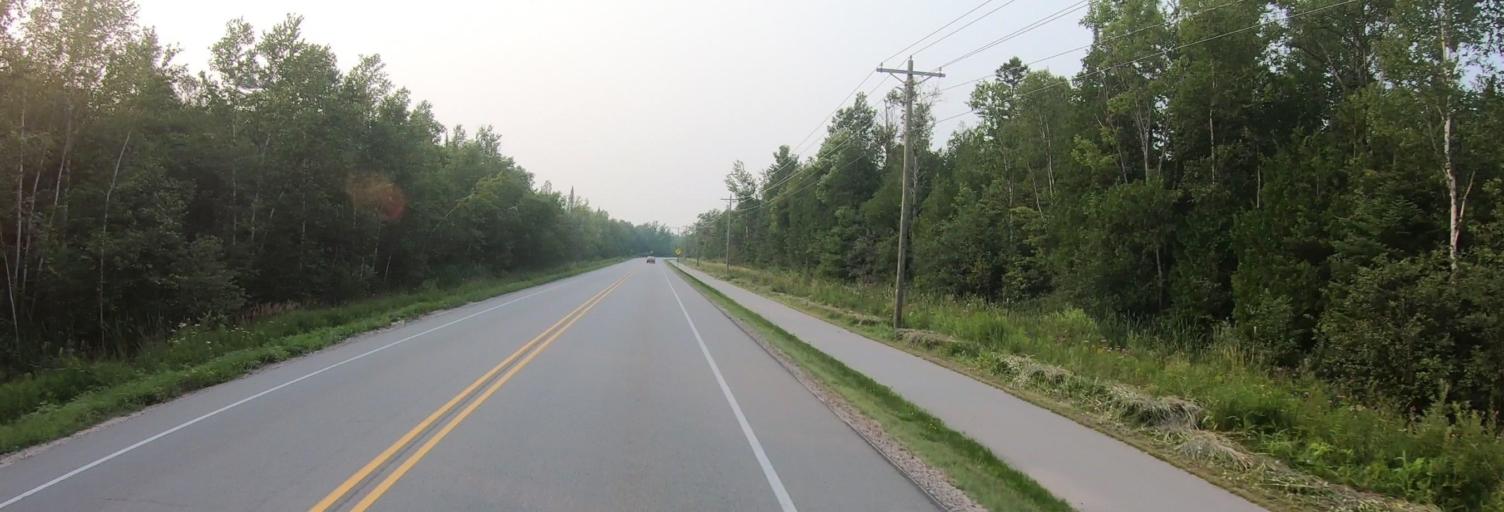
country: US
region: Michigan
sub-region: Chippewa County
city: Sault Ste. Marie
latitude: 46.4281
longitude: -84.6075
